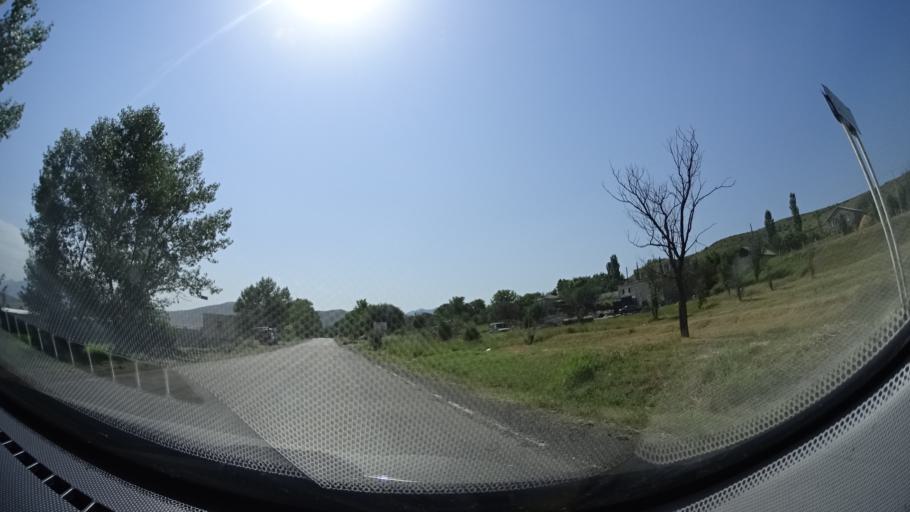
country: GE
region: Samtskhe-Javakheti
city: Akhaltsikhe
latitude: 41.6391
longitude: 43.0314
